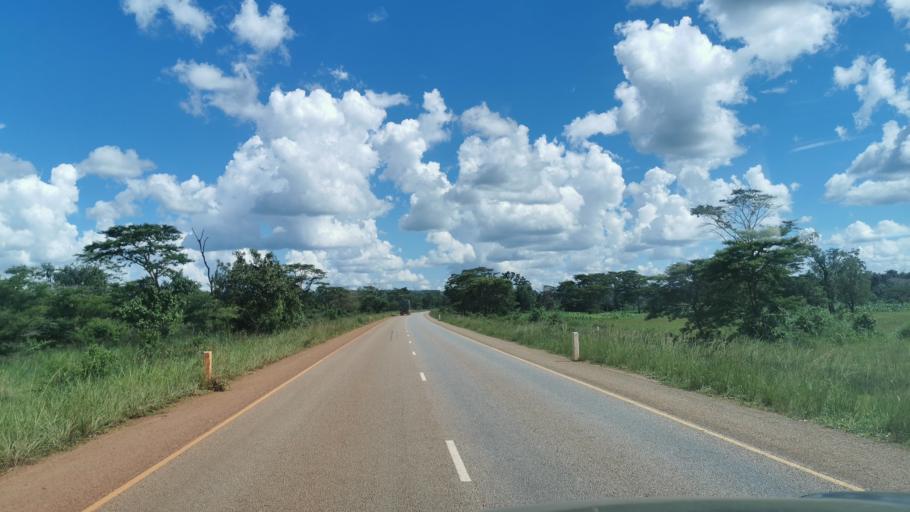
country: TZ
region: Geita
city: Uyovu
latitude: -3.0468
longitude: 31.2497
